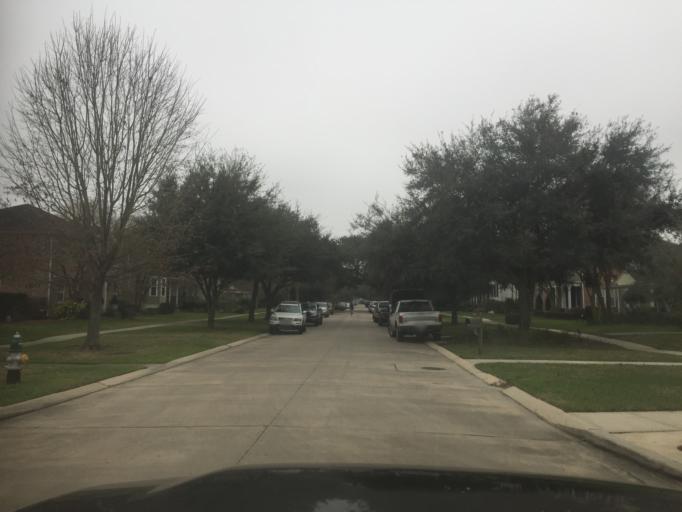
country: US
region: Louisiana
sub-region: Jefferson Parish
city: Metairie
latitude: 29.9988
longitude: -90.1034
